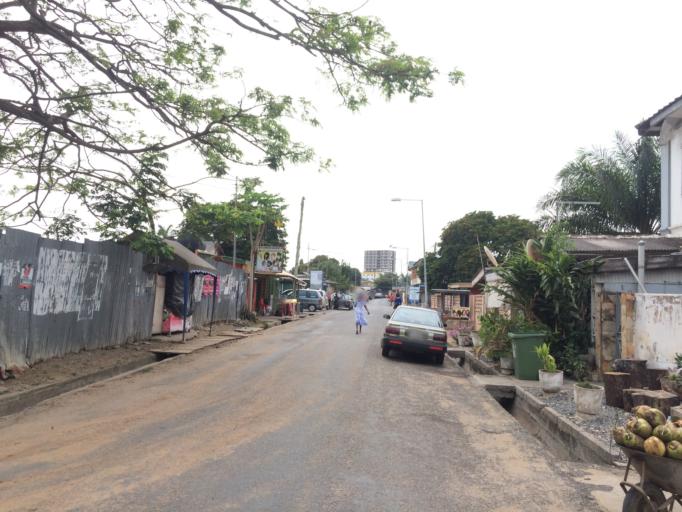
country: GH
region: Greater Accra
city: Accra
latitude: 5.5545
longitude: -0.1803
